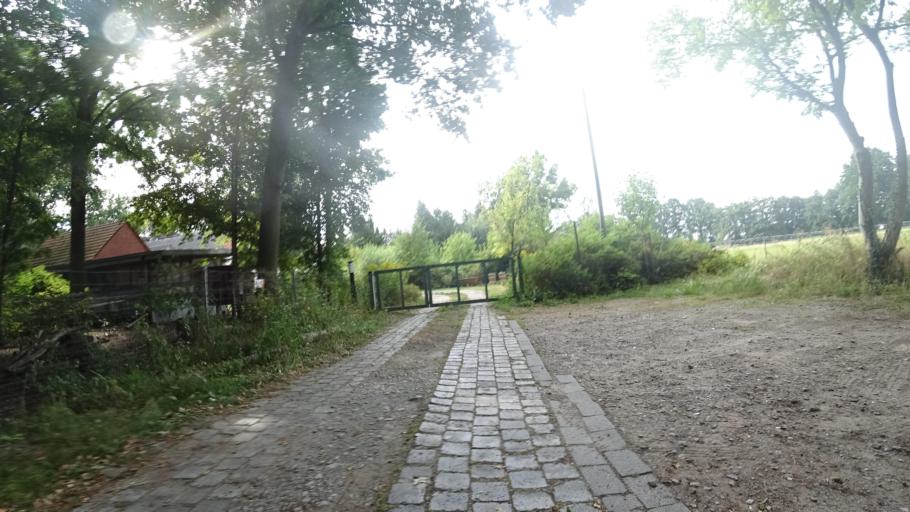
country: DE
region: North Rhine-Westphalia
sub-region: Regierungsbezirk Detmold
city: Guetersloh
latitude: 51.9344
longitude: 8.4091
